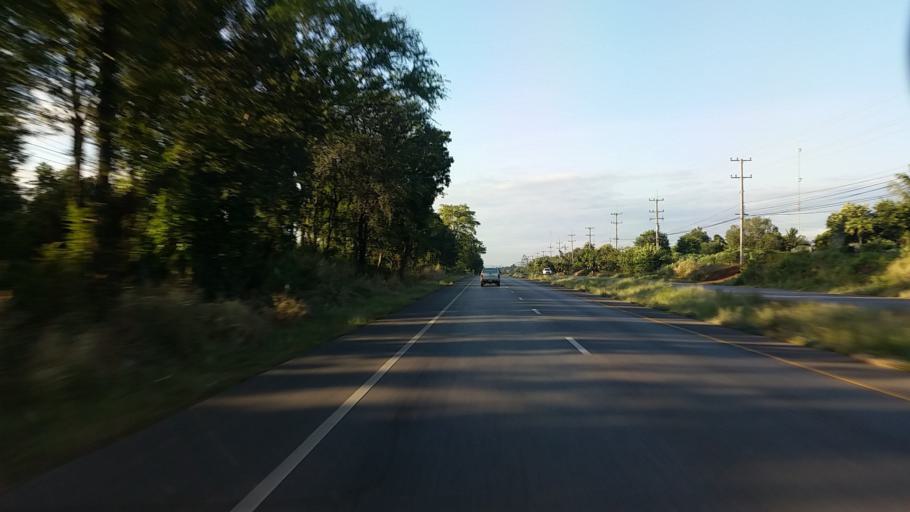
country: TH
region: Lop Buri
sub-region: Amphoe Tha Luang
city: Tha Luang
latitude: 15.1140
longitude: 101.0285
